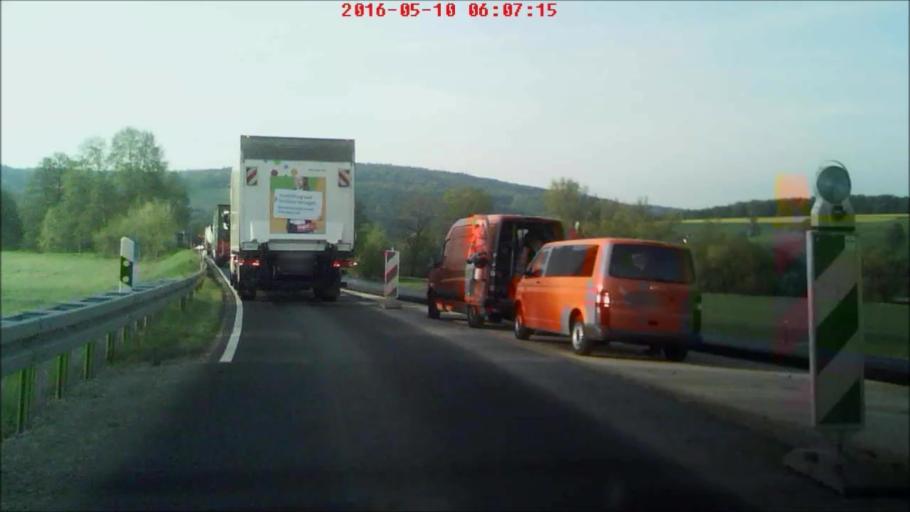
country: DE
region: Hesse
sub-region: Regierungsbezirk Kassel
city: Bad Hersfeld
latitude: 50.8136
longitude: 9.7313
